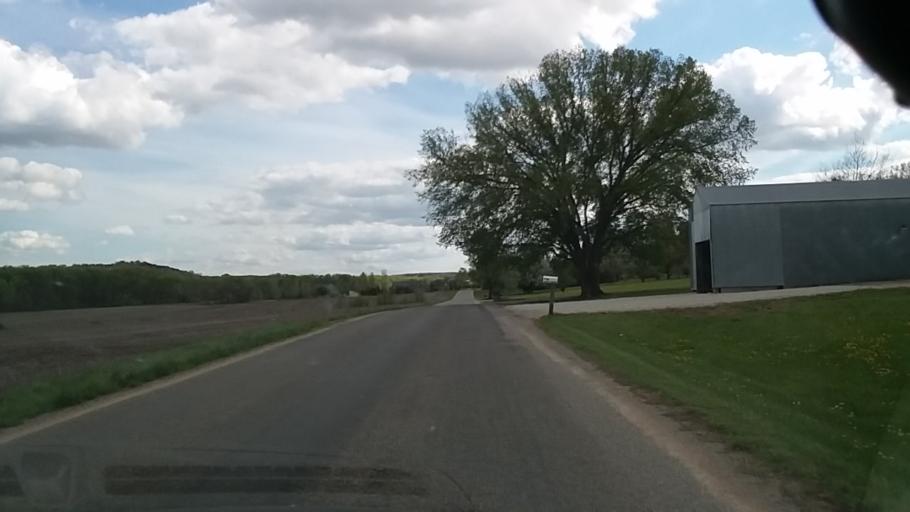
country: US
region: Kansas
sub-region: Douglas County
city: Lawrence
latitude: 38.8959
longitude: -95.2557
